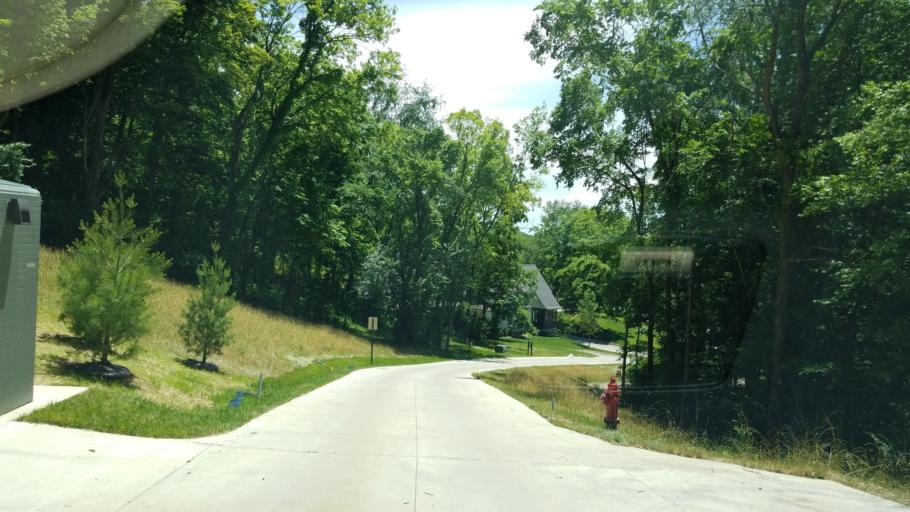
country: US
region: Tennessee
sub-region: Williamson County
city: Brentwood
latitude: 36.0529
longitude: -86.8117
